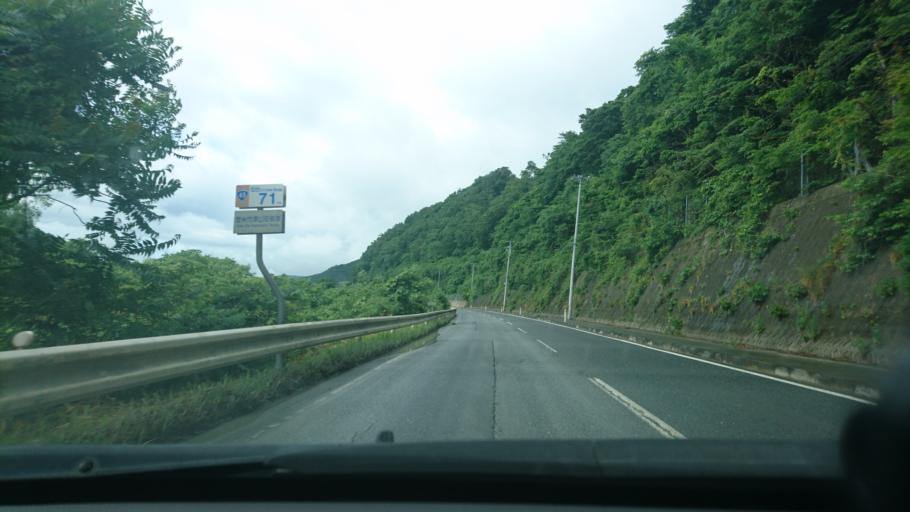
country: JP
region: Miyagi
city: Ishinomaki
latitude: 38.5825
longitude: 141.3037
